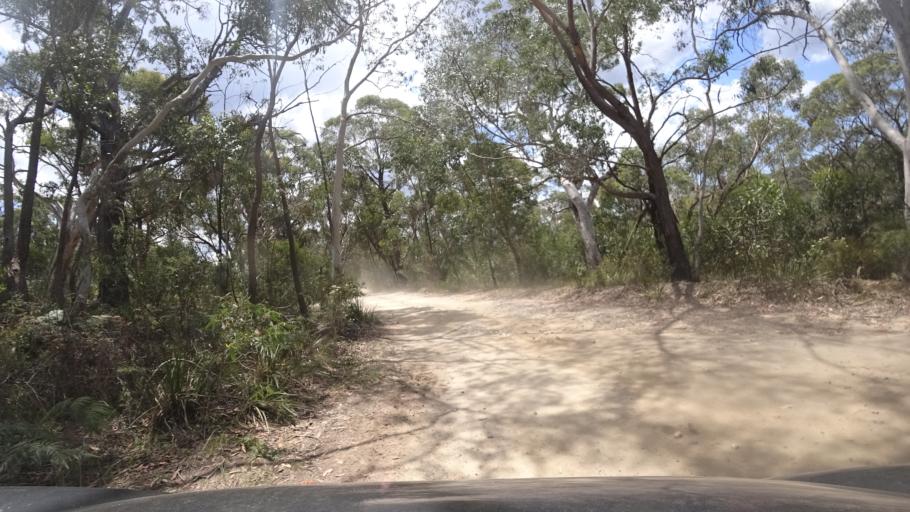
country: AU
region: New South Wales
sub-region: Lithgow
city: Lithgow
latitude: -33.4804
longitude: 150.2466
